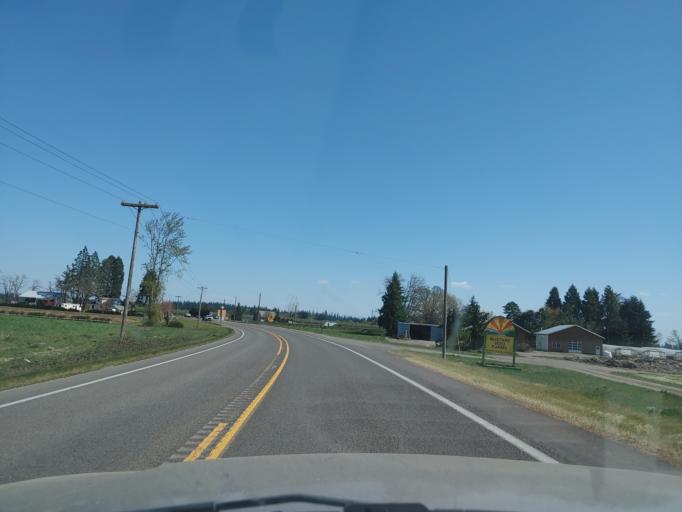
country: US
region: Oregon
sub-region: Yamhill County
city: Newberg
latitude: 45.2350
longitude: -122.9138
